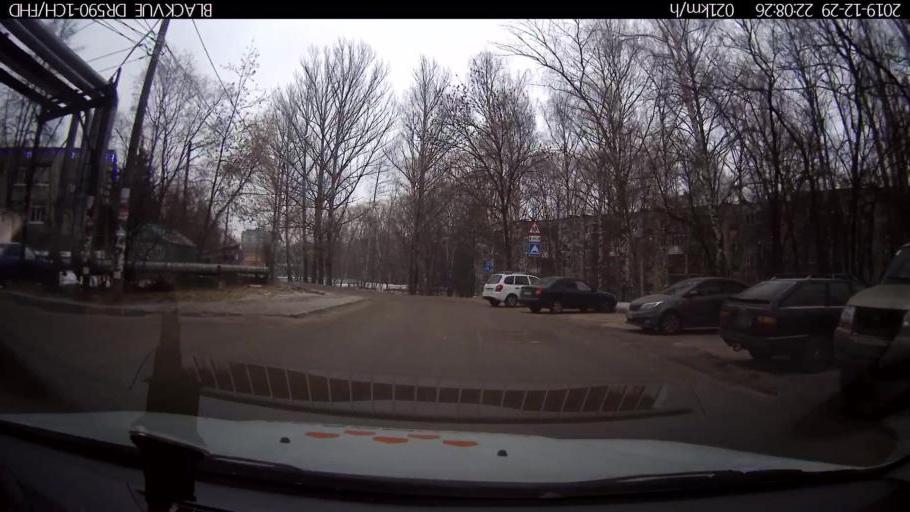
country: RU
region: Nizjnij Novgorod
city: Nizhniy Novgorod
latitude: 56.2301
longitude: 43.9498
